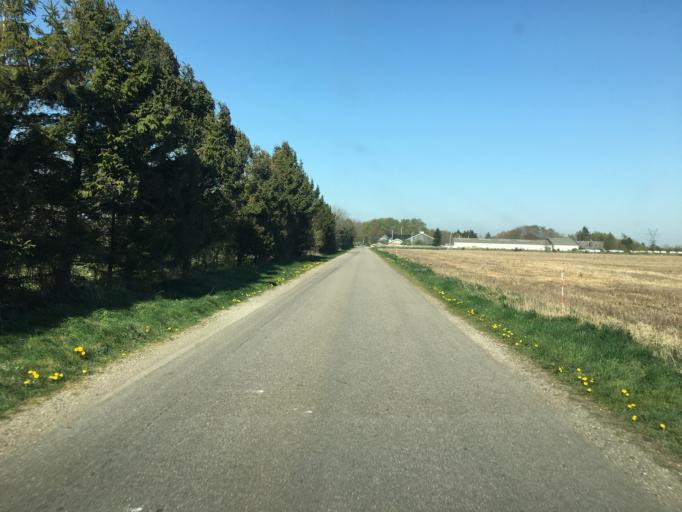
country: DK
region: South Denmark
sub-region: Aabenraa Kommune
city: Rodekro
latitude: 55.0864
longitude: 9.2708
